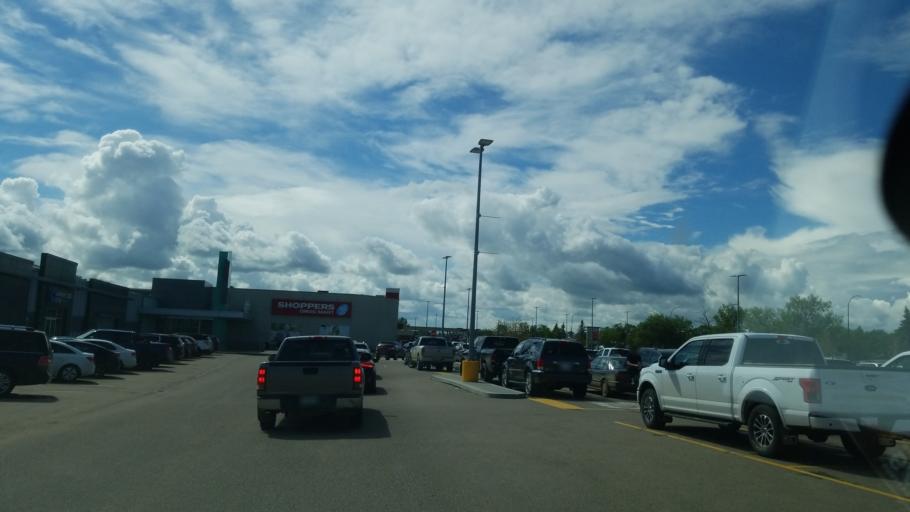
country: CA
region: Saskatchewan
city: Lloydminster
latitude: 53.2771
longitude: -110.0110
